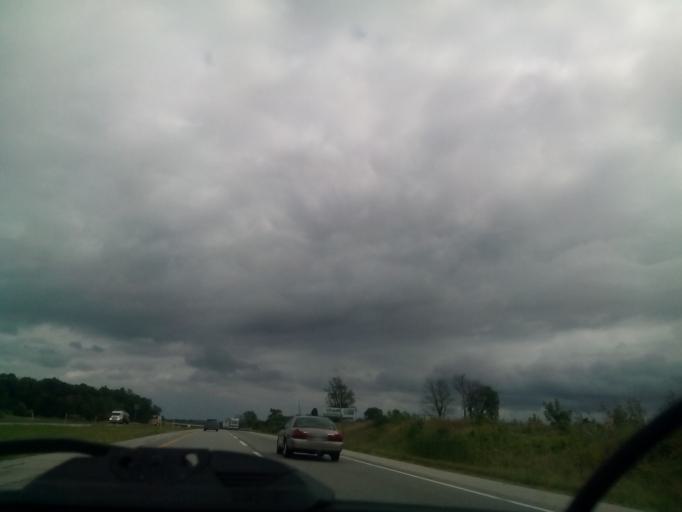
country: US
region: Indiana
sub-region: Steuben County
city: Fremont
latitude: 41.6795
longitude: -84.8763
